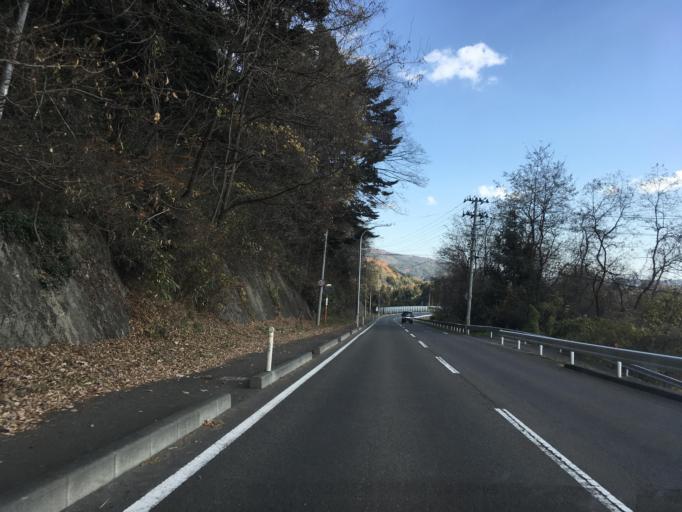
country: JP
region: Miyagi
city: Sendai
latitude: 38.2799
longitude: 140.7607
